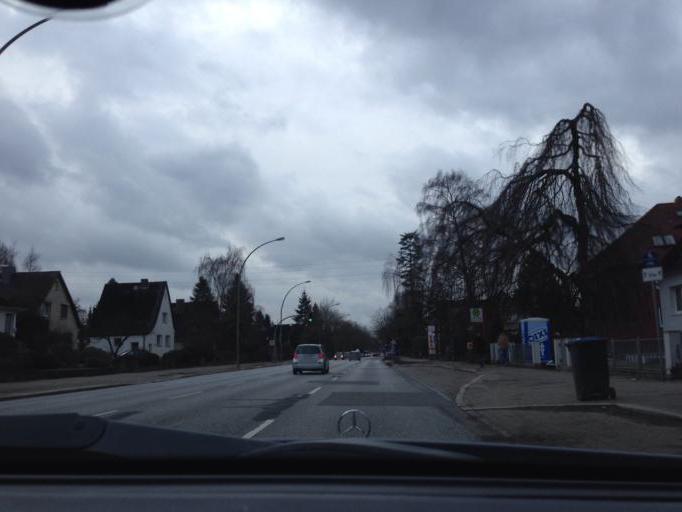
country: DE
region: Hamburg
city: Farmsen-Berne
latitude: 53.5923
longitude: 10.1315
